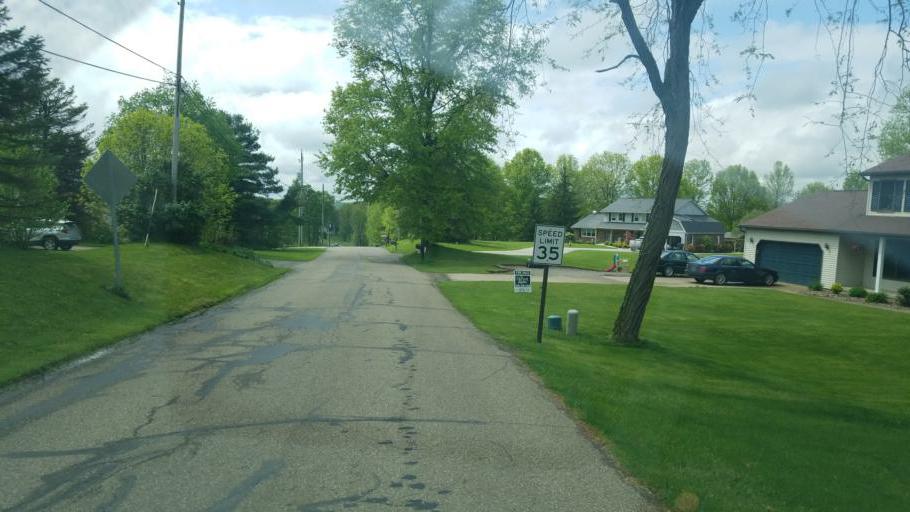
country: US
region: Ohio
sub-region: Tuscarawas County
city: Strasburg
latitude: 40.6315
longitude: -81.4168
